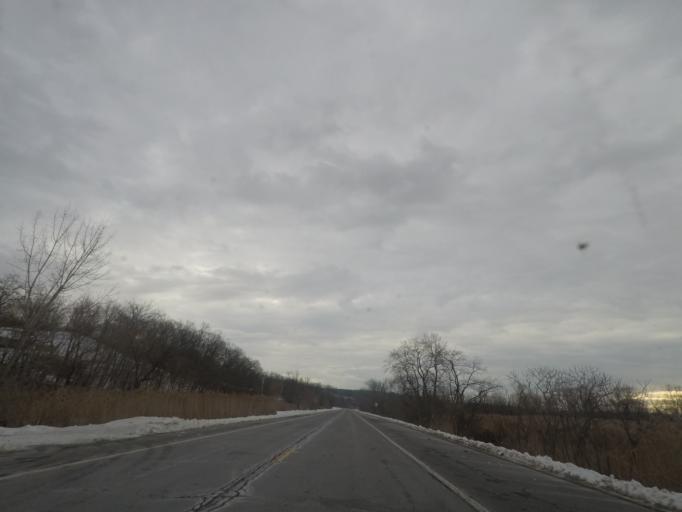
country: US
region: New York
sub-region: Rensselaer County
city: East Greenbush
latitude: 42.5806
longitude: -73.7392
